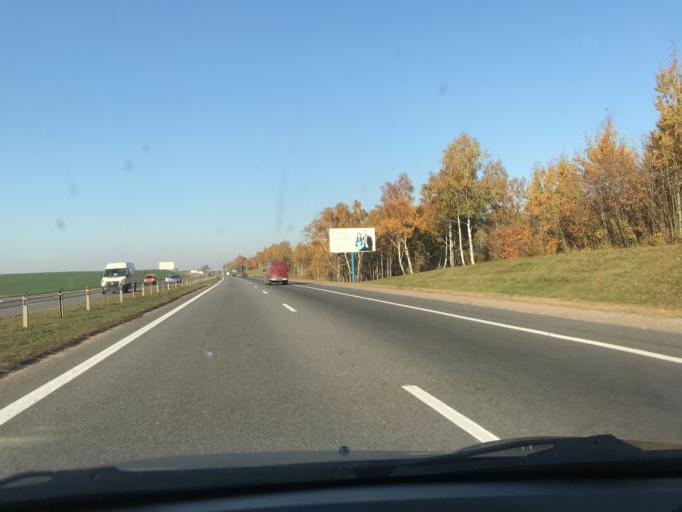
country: BY
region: Minsk
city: Samakhvalavichy
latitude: 53.7706
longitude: 27.5225
